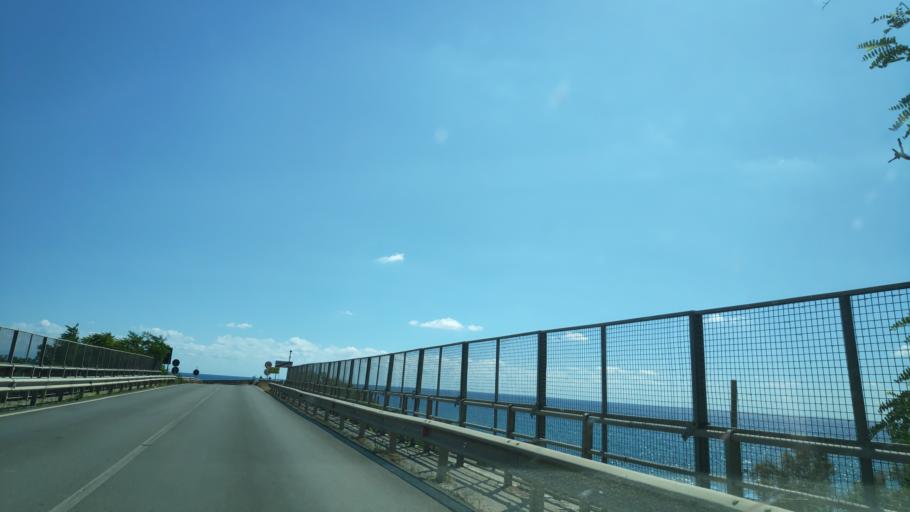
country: IT
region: Calabria
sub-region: Provincia di Cosenza
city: Campora San Giovanni
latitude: 39.0664
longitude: 16.0919
